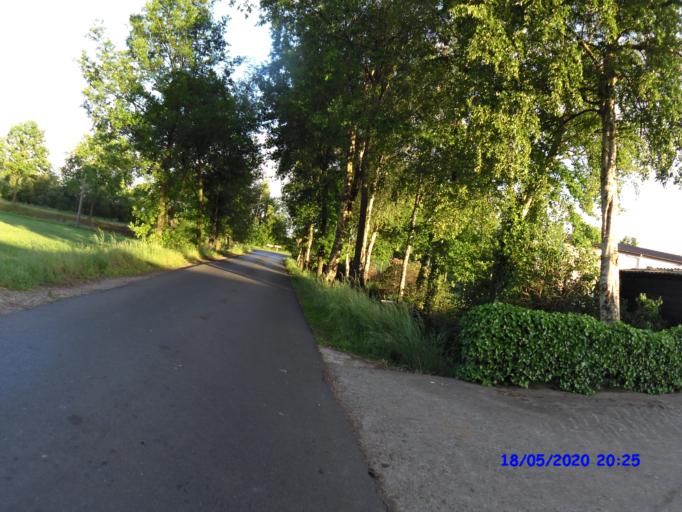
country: BE
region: Flanders
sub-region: Provincie Antwerpen
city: Kasterlee
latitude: 51.1999
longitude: 4.9314
